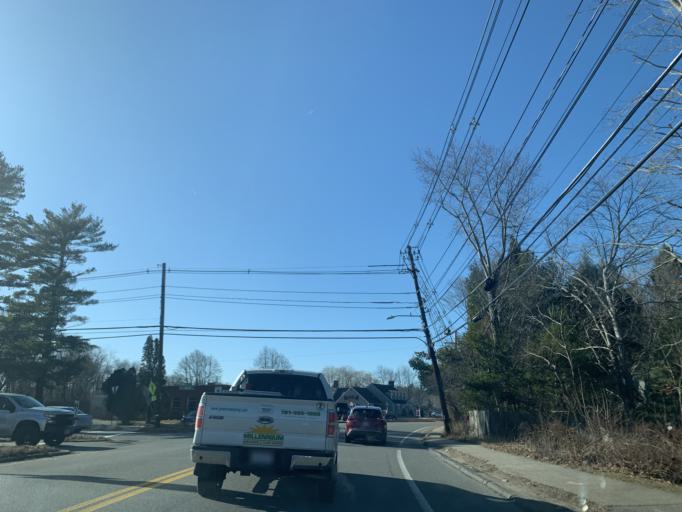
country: US
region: Massachusetts
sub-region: Middlesex County
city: Sudbury
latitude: 42.3613
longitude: -71.4015
